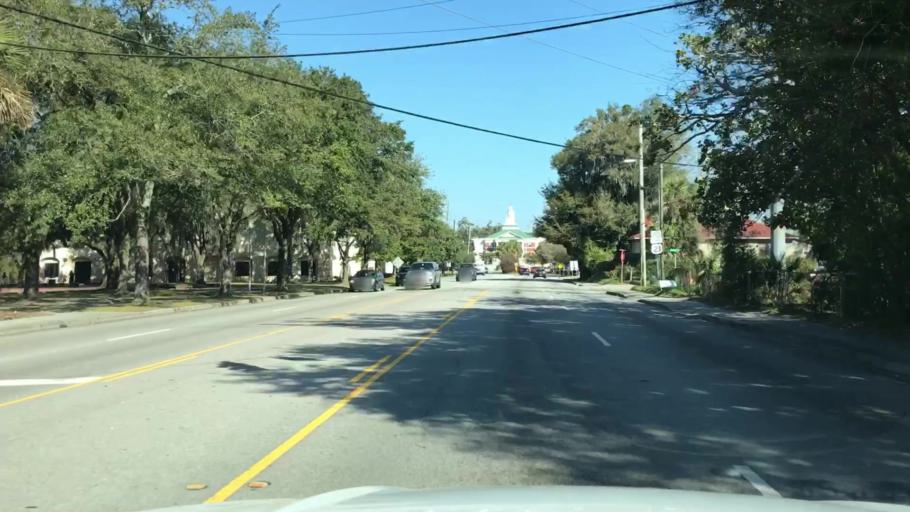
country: US
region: South Carolina
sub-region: Beaufort County
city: Beaufort
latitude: 32.4376
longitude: -80.6859
